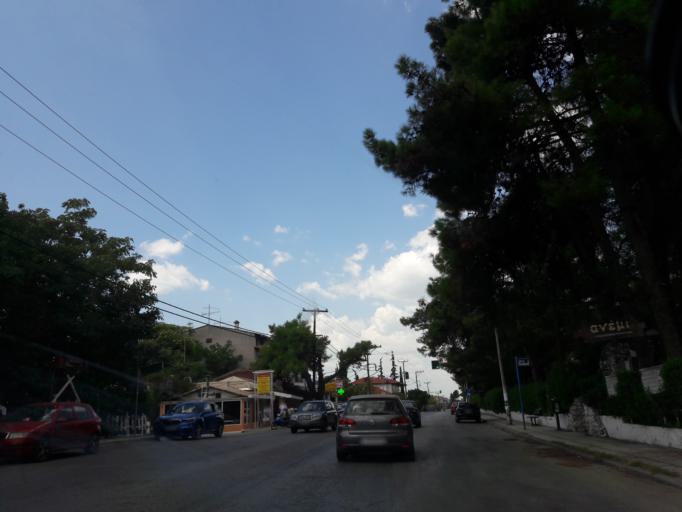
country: GR
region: Central Macedonia
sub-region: Nomos Thessalonikis
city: Thermi
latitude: 40.5240
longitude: 23.0507
